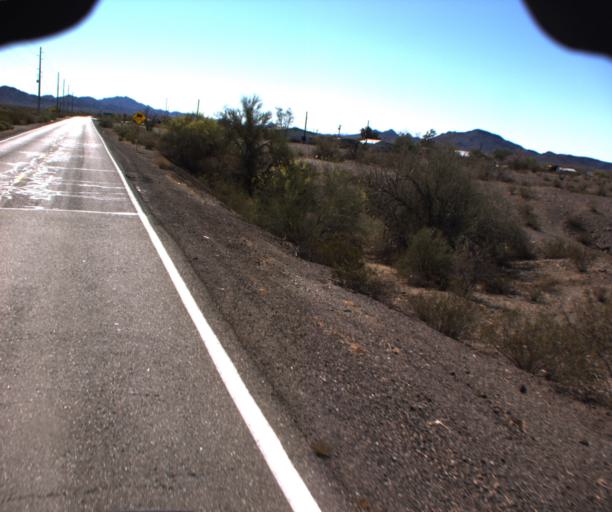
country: US
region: Arizona
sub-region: La Paz County
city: Salome
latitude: 33.7452
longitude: -113.7559
